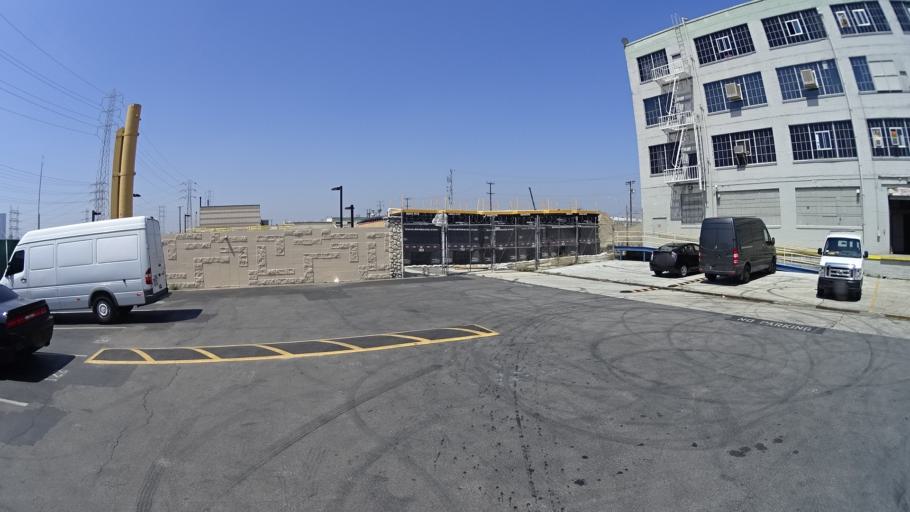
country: US
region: California
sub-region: Los Angeles County
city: Boyle Heights
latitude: 34.0359
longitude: -118.2262
